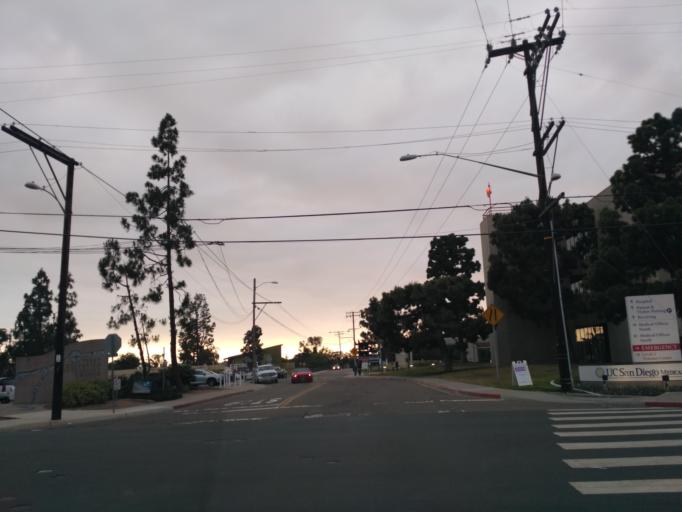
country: US
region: California
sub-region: San Diego County
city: San Diego
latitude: 32.7538
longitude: -117.1648
